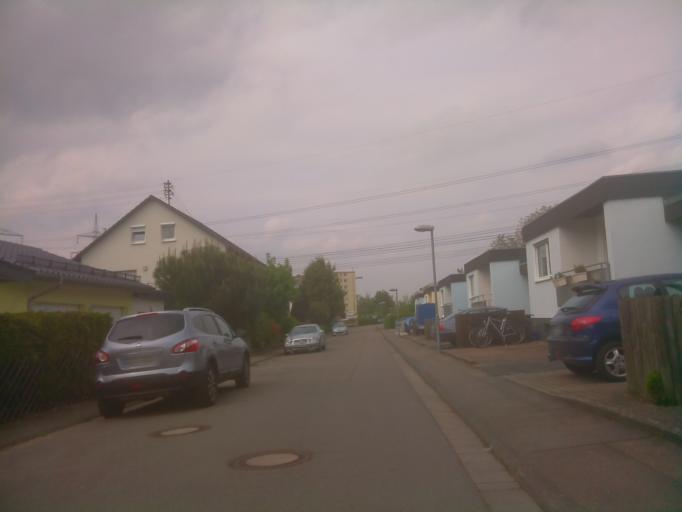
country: DE
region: Baden-Wuerttemberg
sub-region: Karlsruhe Region
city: Sandhausen
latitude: 49.3456
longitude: 8.6680
